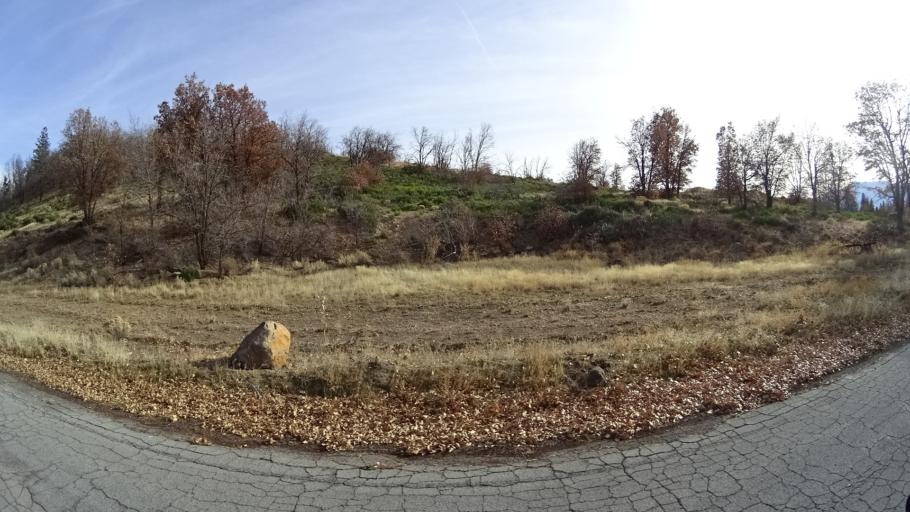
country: US
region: California
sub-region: Siskiyou County
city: Weed
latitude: 41.4441
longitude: -122.3849
